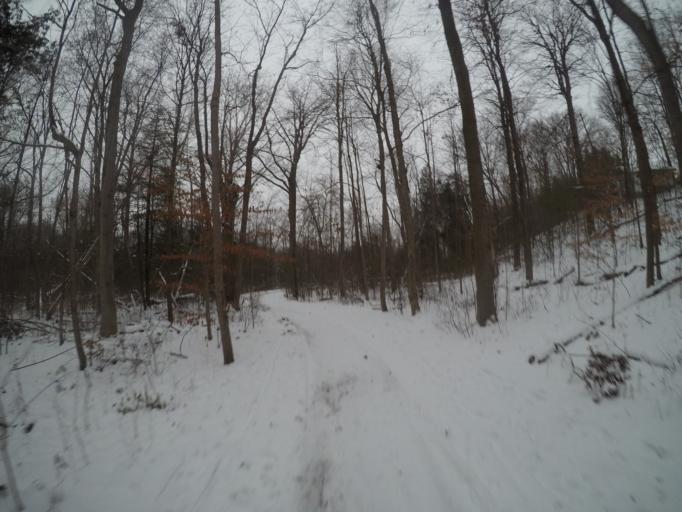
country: CA
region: Ontario
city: Waterloo
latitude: 43.4868
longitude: -80.5090
